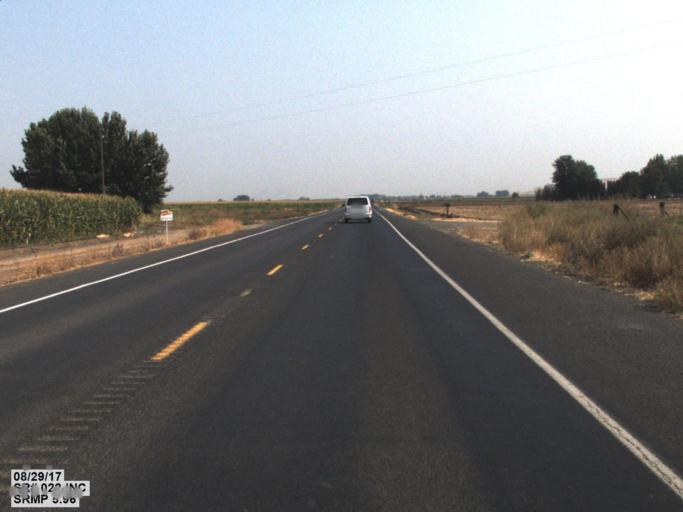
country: US
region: Washington
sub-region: Yakima County
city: Toppenish
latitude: 46.3535
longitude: -120.2868
